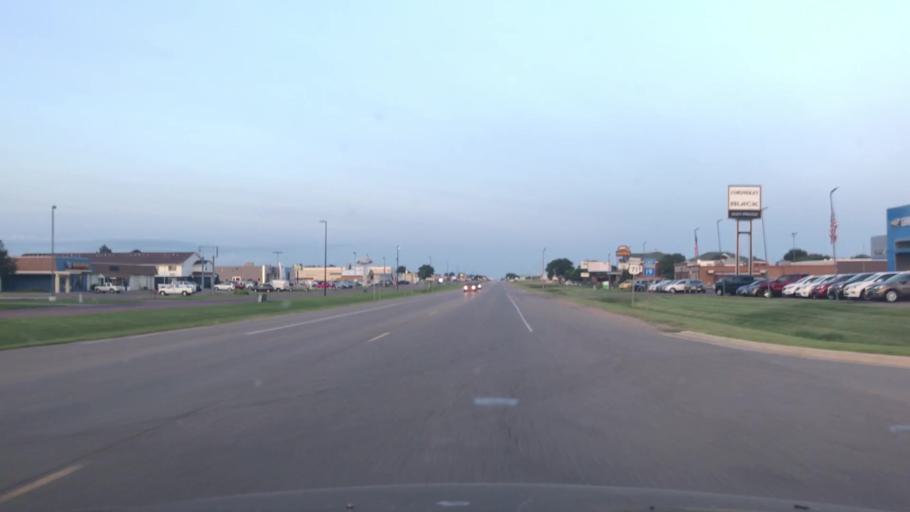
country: US
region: Minnesota
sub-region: Redwood County
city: Redwood Falls
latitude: 44.5414
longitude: -95.0959
